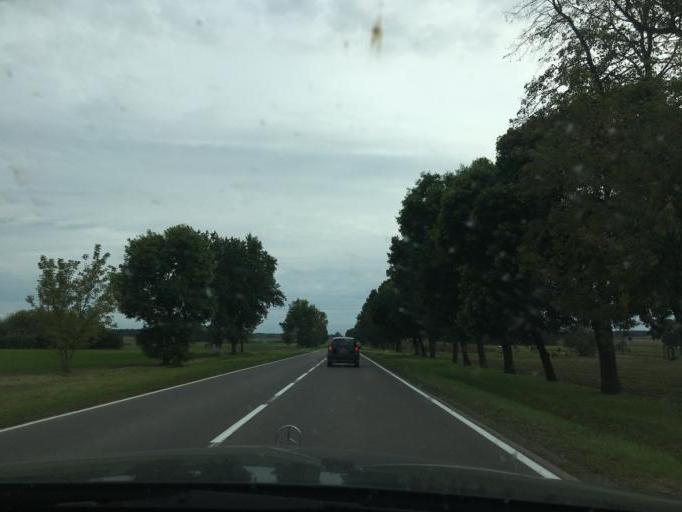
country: PL
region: Masovian Voivodeship
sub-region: Powiat ostrowski
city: Ostrow Mazowiecka
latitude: 52.8816
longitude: 21.8648
